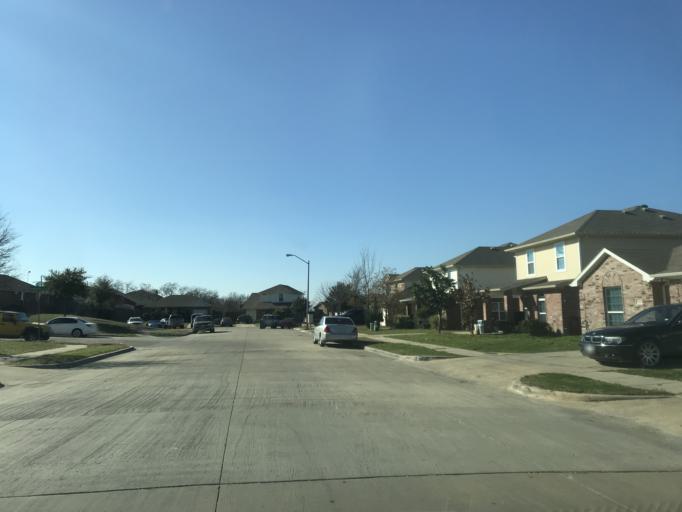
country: US
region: Texas
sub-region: Dallas County
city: Cockrell Hill
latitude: 32.7702
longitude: -96.9053
